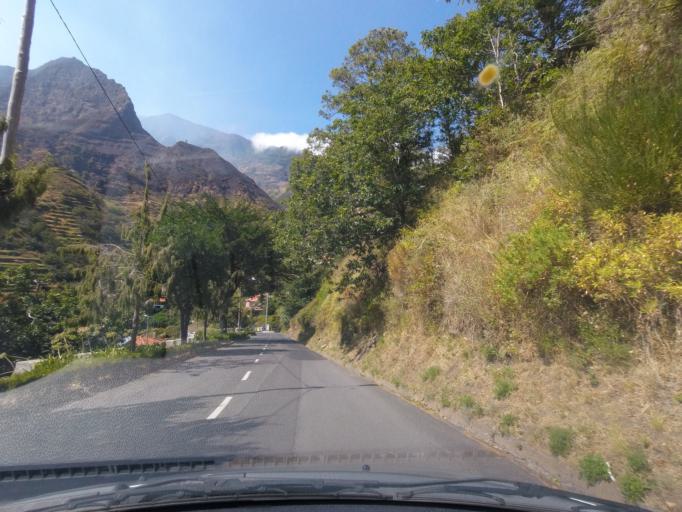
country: PT
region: Madeira
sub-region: Camara de Lobos
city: Curral das Freiras
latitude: 32.7314
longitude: -17.0251
